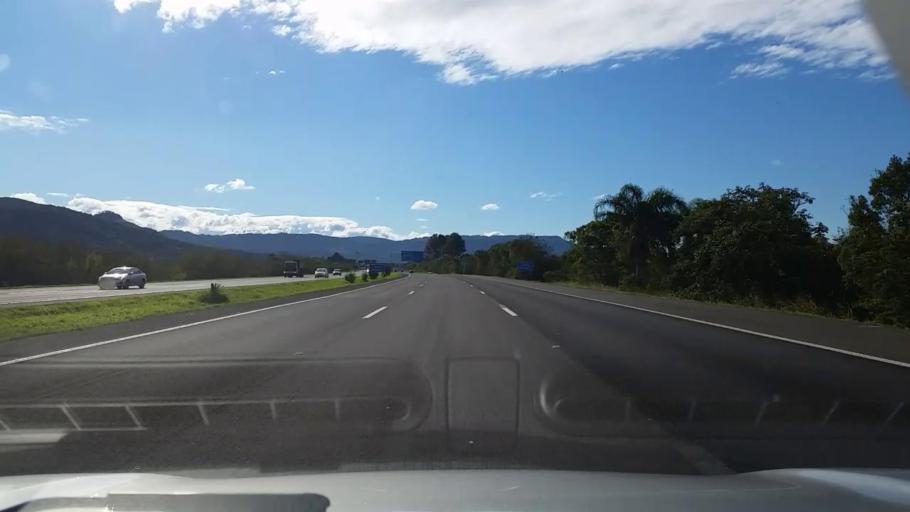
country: BR
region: Rio Grande do Sul
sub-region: Osorio
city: Osorio
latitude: -29.8890
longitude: -50.4590
